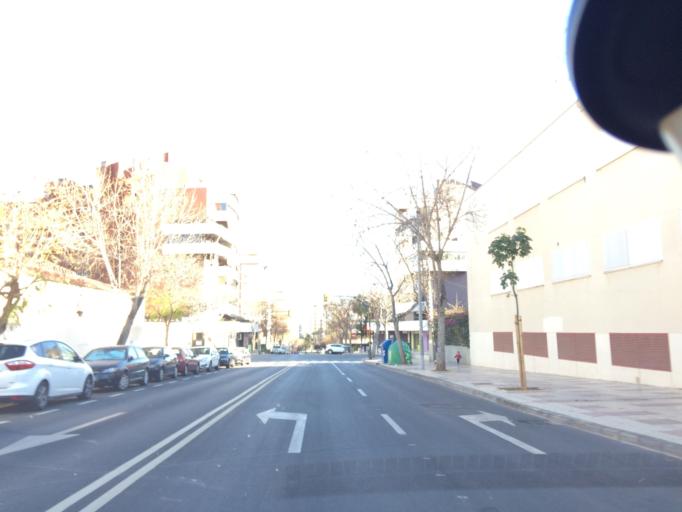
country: ES
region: Andalusia
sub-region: Provincia de Malaga
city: Malaga
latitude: 36.7243
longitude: -4.4417
